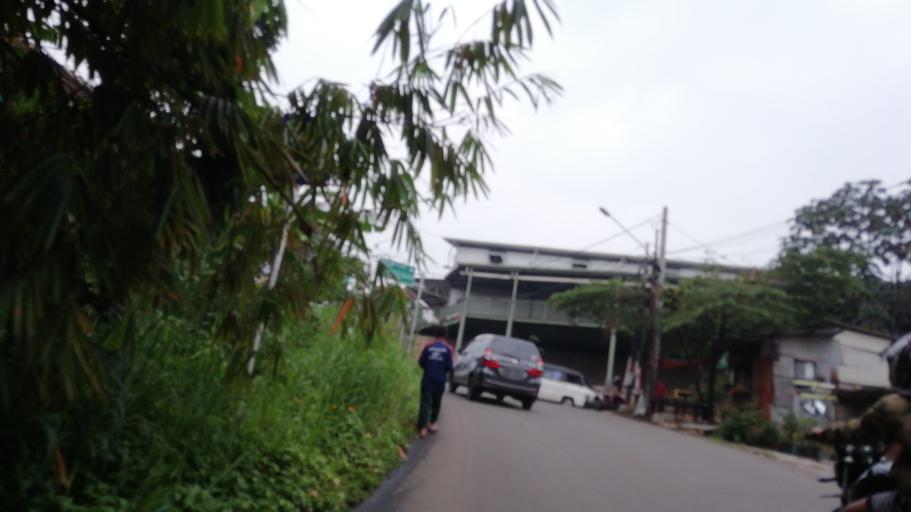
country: ID
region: West Java
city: Bogor
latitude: -6.5333
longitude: 106.8062
